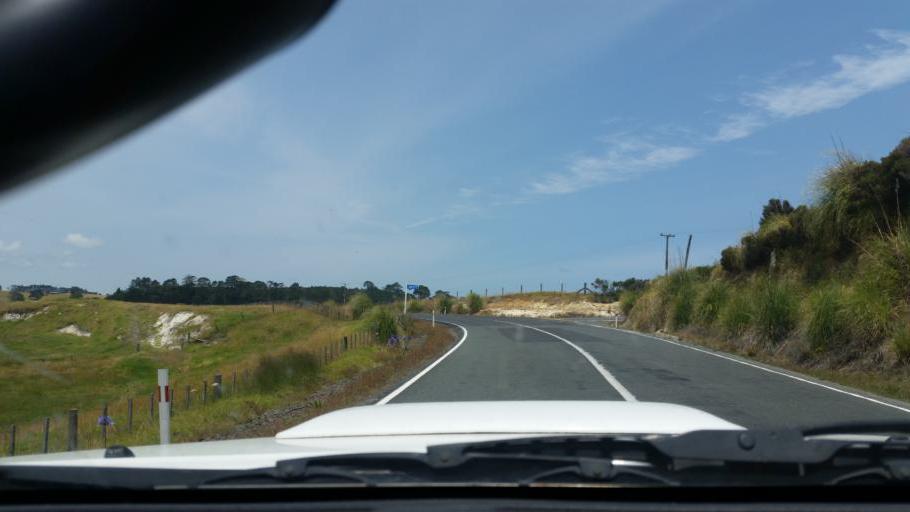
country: NZ
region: Northland
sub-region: Kaipara District
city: Dargaville
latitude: -36.1872
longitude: 174.0330
